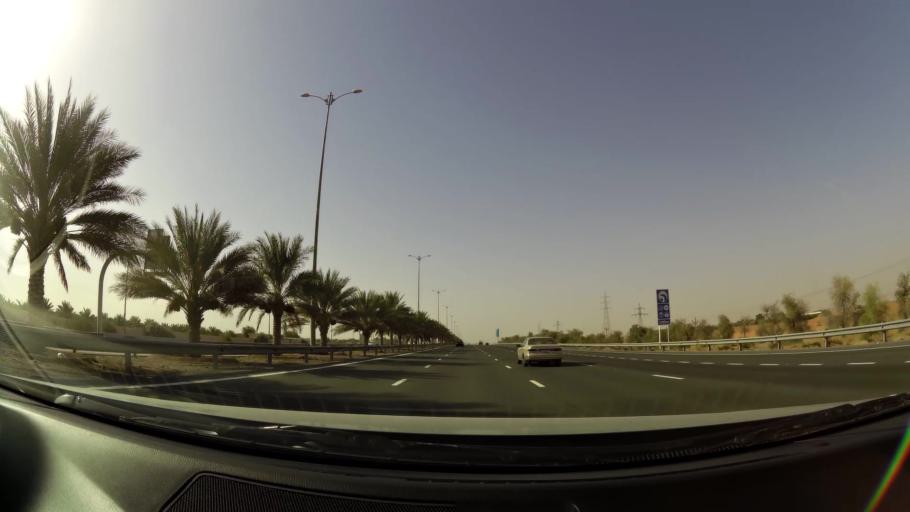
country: OM
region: Al Buraimi
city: Al Buraymi
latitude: 24.4770
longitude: 55.7757
